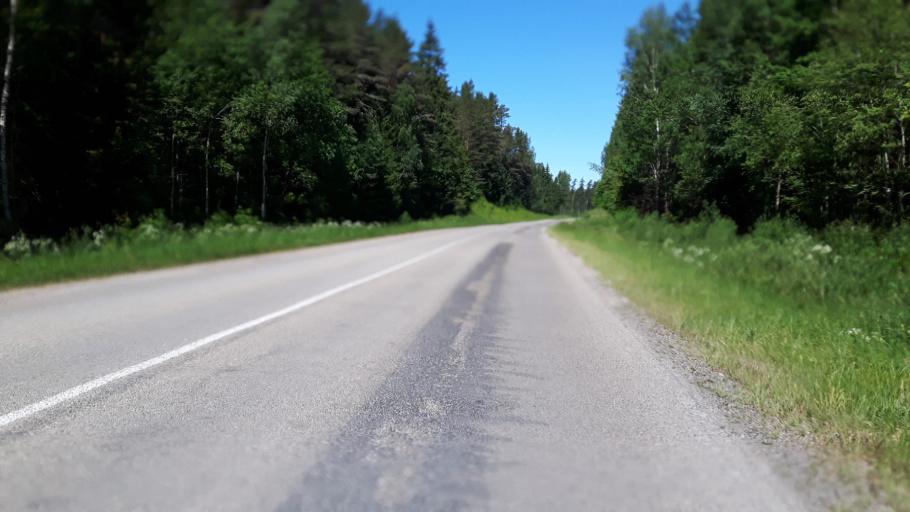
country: LV
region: Tukuma Rajons
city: Tukums
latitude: 57.0076
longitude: 23.0599
